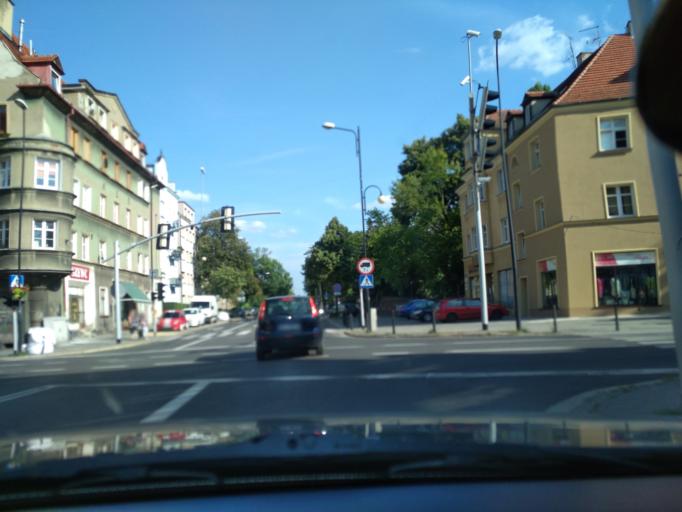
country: PL
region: Silesian Voivodeship
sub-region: Gliwice
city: Gliwice
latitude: 50.2954
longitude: 18.6520
